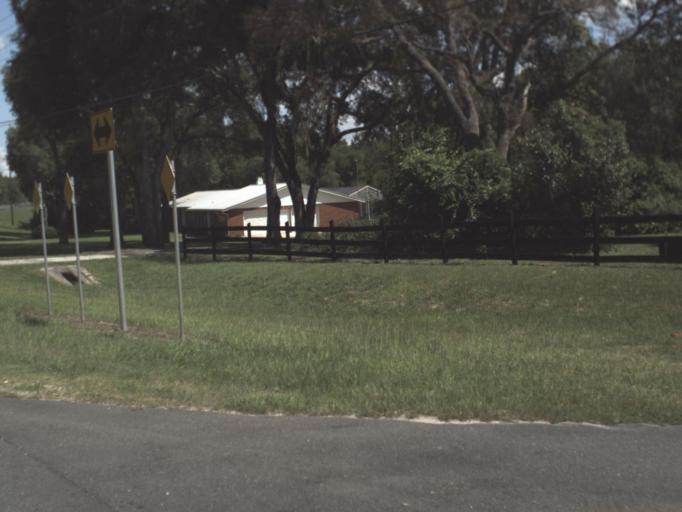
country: US
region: Florida
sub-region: Clay County
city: Keystone Heights
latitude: 29.7479
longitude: -81.9927
